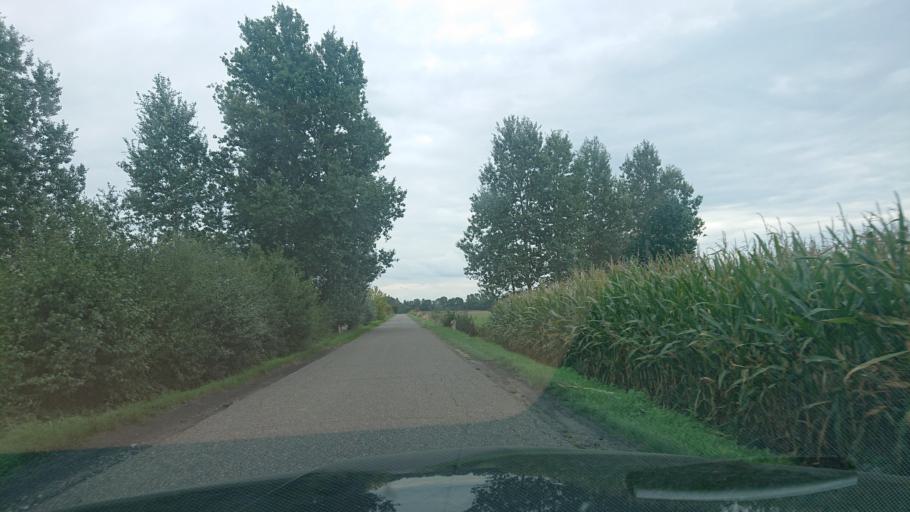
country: PL
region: Greater Poland Voivodeship
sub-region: Powiat gnieznienski
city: Niechanowo
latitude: 52.4641
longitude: 17.6209
